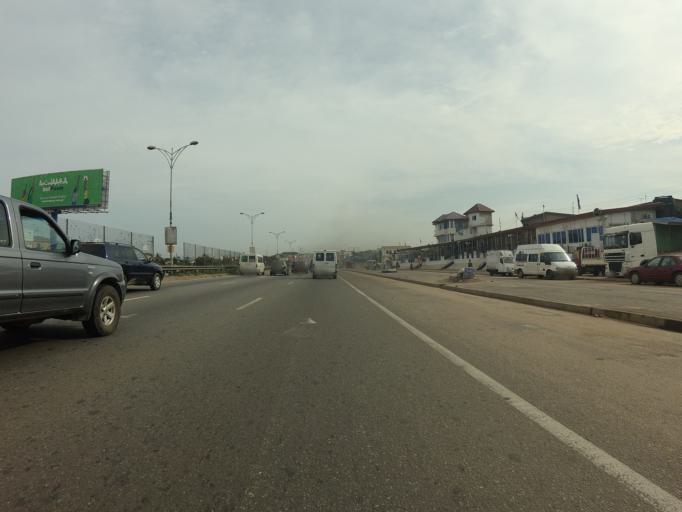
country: GH
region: Greater Accra
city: Gbawe
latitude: 5.5925
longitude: -0.2677
